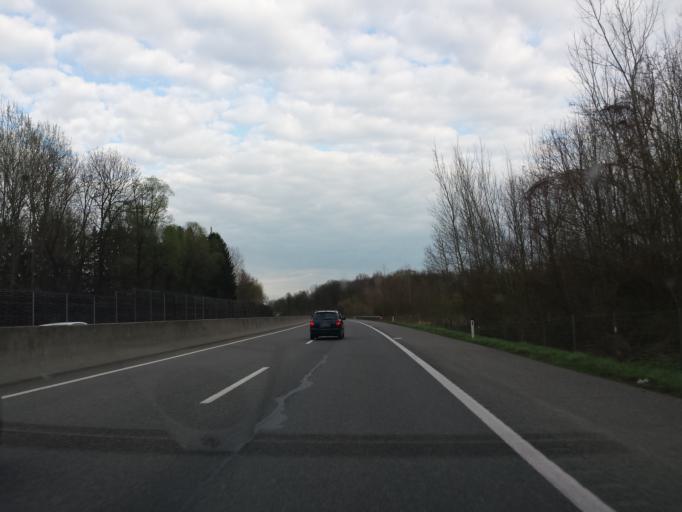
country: AT
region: Lower Austria
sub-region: Politischer Bezirk Tulln
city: Michelhausen
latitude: 48.3690
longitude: 15.9424
